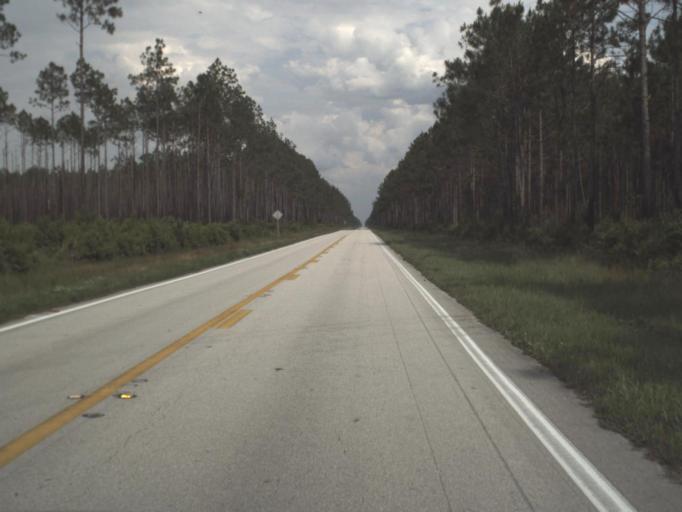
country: US
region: Florida
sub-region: Baker County
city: Macclenny
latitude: 30.5621
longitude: -82.3883
